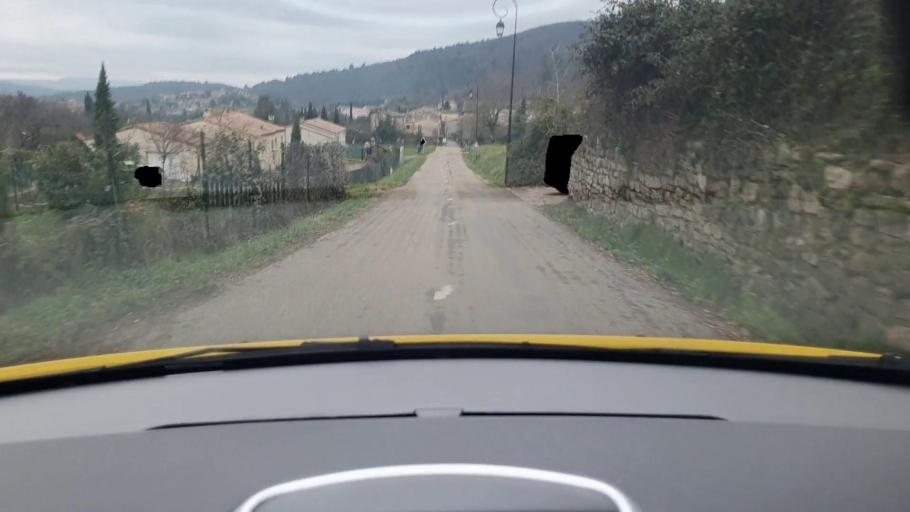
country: FR
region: Languedoc-Roussillon
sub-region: Departement du Gard
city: Molieres-sur-Ceze
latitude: 44.3048
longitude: 4.1482
